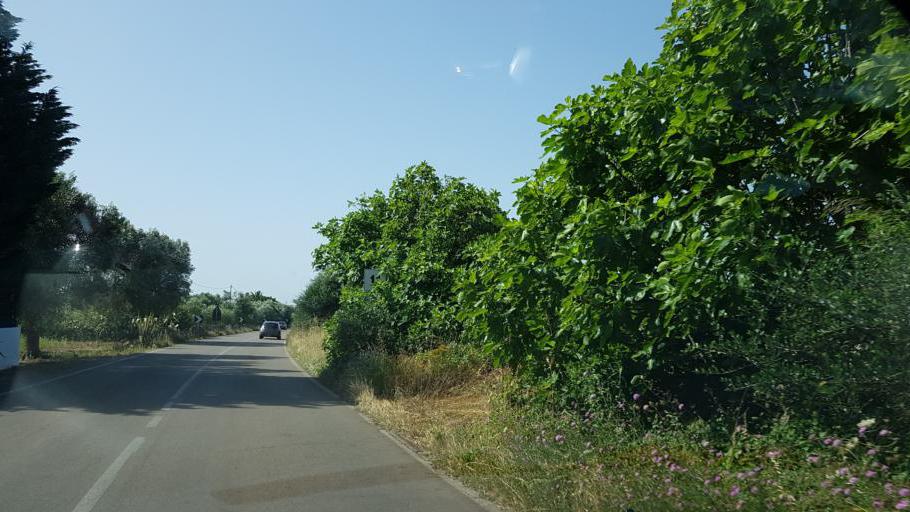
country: IT
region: Apulia
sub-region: Provincia di Lecce
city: Porto Cesareo
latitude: 40.3120
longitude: 17.8629
